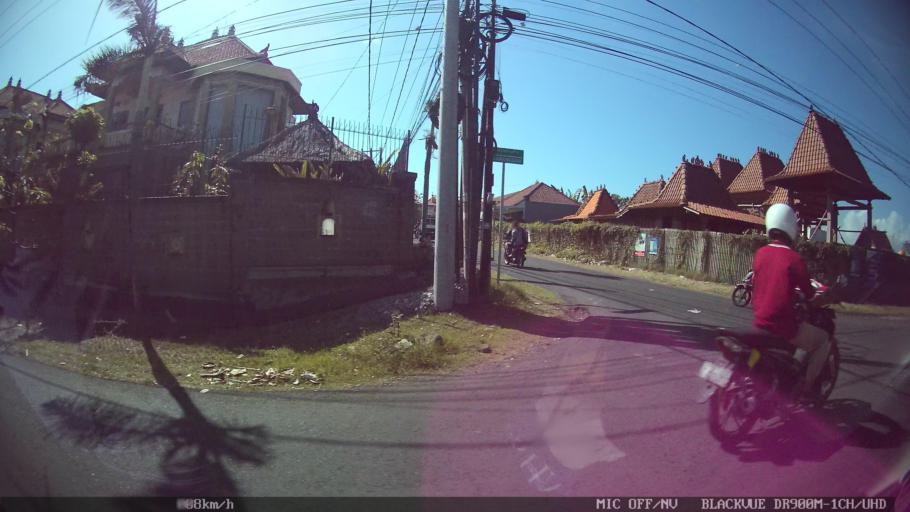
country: ID
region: Bali
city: Banjar Kertasari
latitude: -8.6331
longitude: 115.1891
